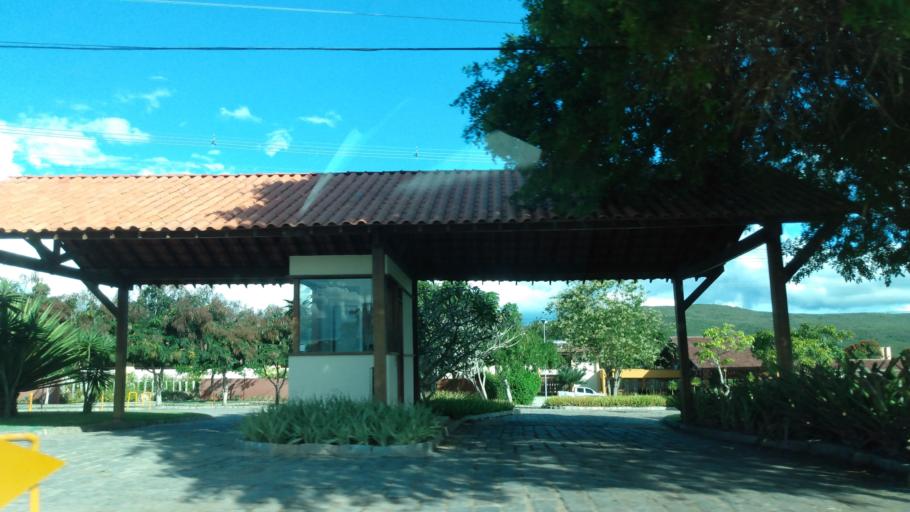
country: BR
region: Pernambuco
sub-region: Gravata
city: Gravata
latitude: -8.2009
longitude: -35.5904
